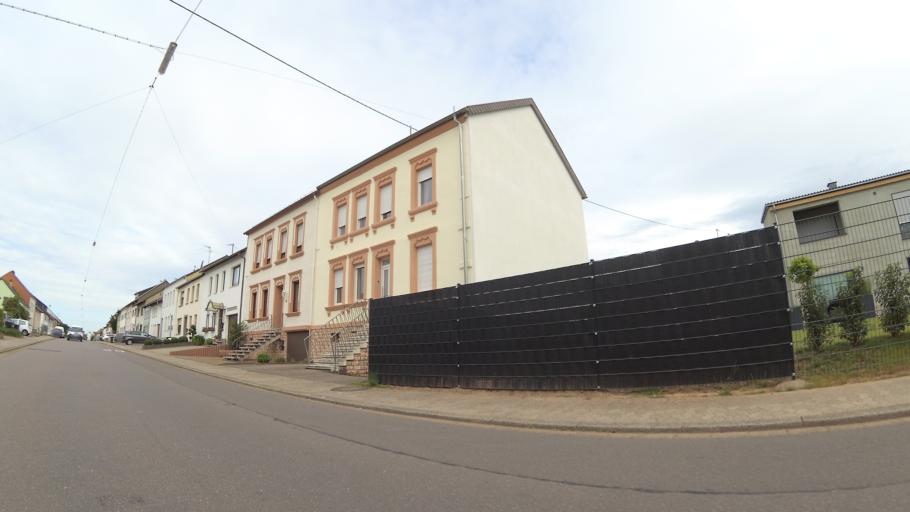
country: DE
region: Saarland
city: Schwalbach
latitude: 49.3217
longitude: 6.8219
